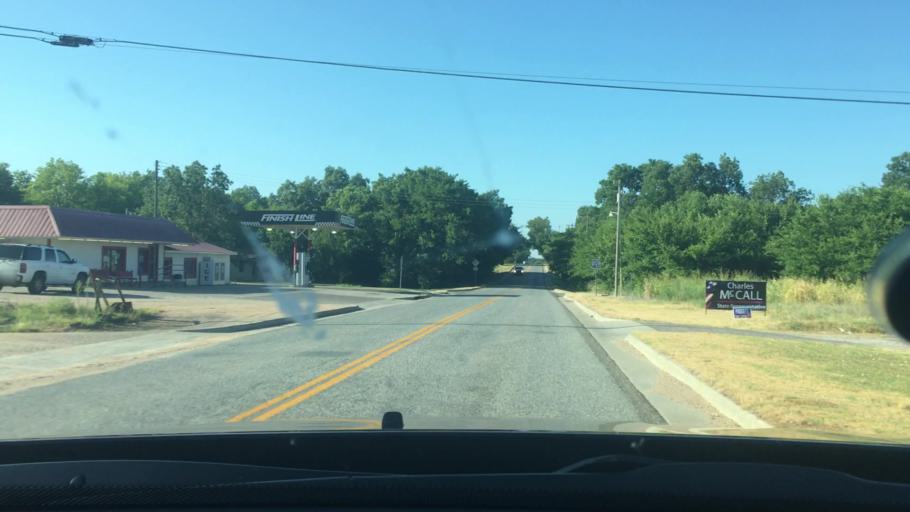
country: US
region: Oklahoma
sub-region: Murray County
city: Sulphur
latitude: 34.4038
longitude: -96.8271
